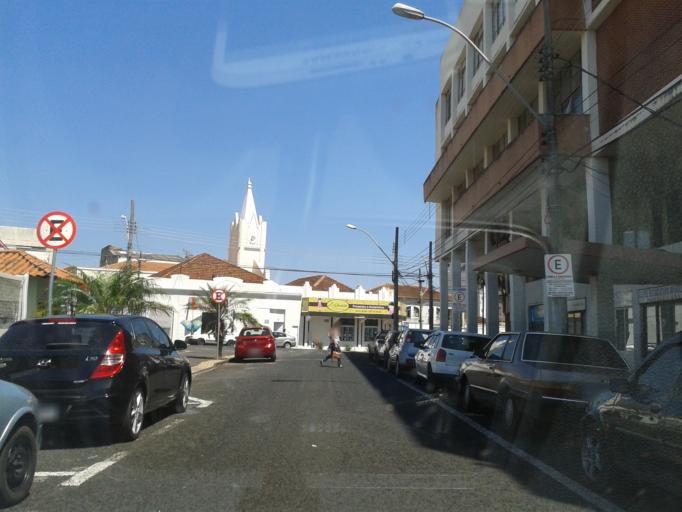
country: BR
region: Minas Gerais
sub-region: Araguari
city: Araguari
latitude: -18.6492
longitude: -48.1895
